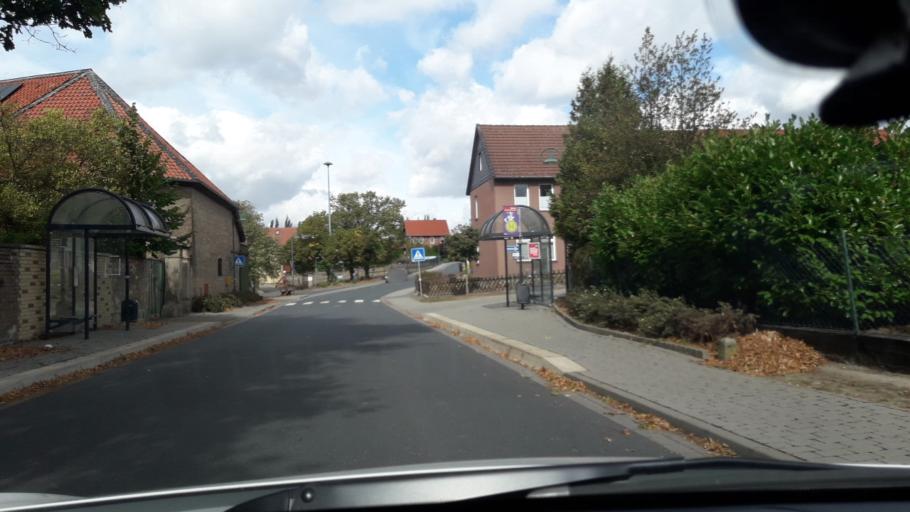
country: DE
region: Lower Saxony
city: Elbe
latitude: 52.0742
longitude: 10.3298
